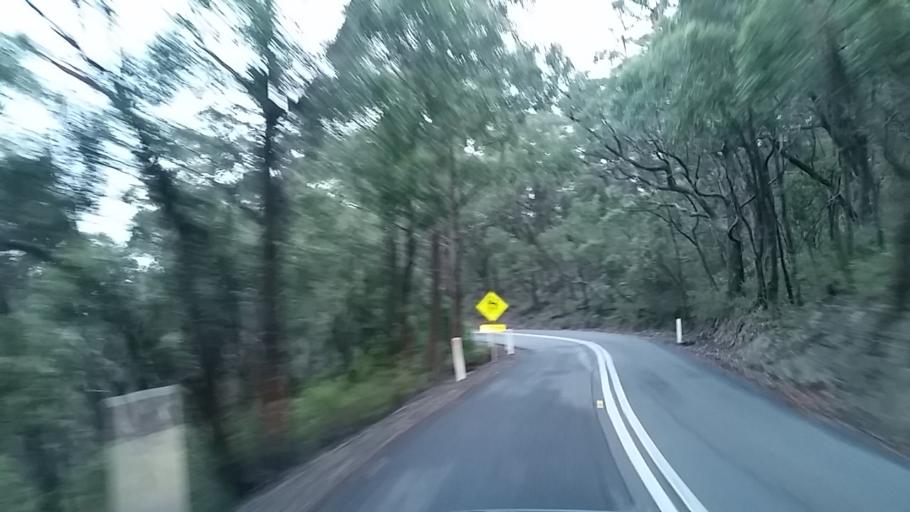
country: AU
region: South Australia
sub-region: Adelaide Hills
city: Crafers
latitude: -34.9749
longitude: 138.7076
